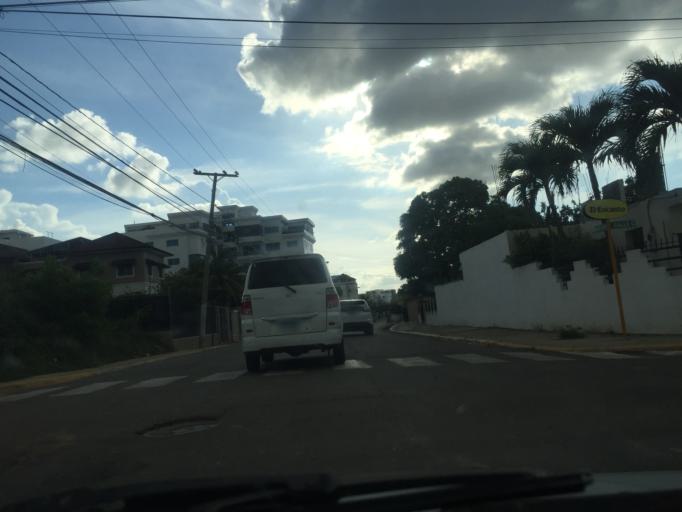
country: DO
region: Santiago
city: Santiago de los Caballeros
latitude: 19.4349
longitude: -70.6659
